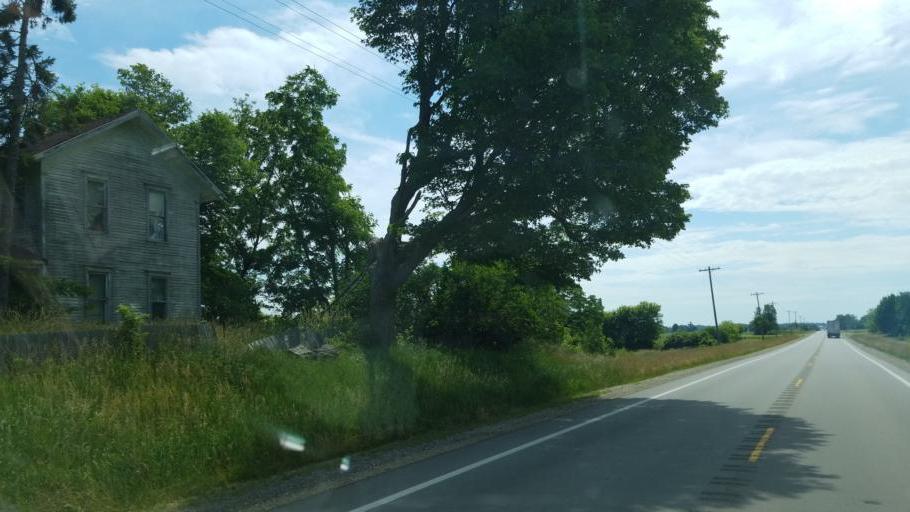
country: US
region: Michigan
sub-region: Eaton County
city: Charlotte
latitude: 42.6499
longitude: -84.8983
